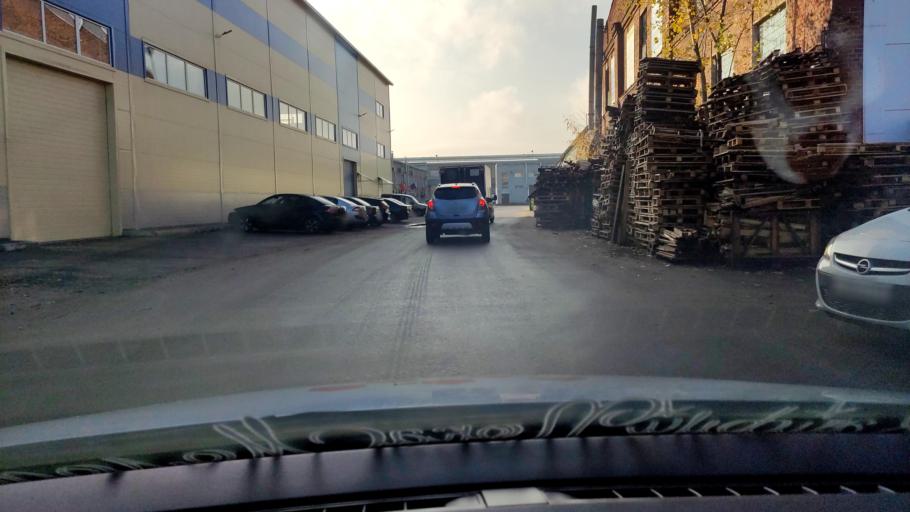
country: RU
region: Voronezj
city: Voronezh
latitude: 51.6902
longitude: 39.1754
